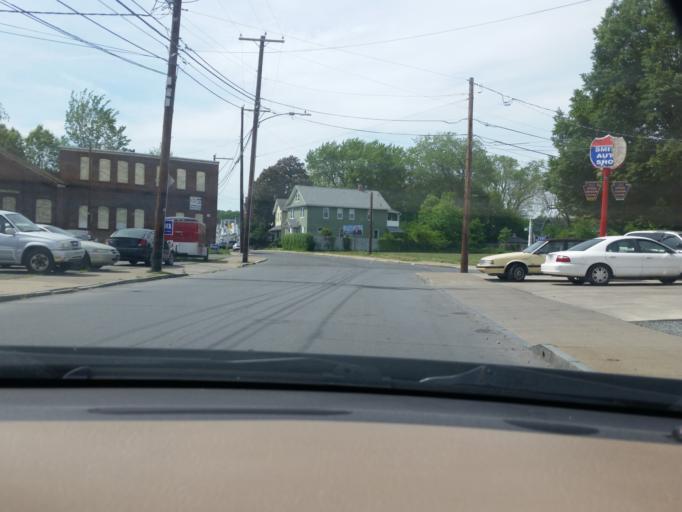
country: US
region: Pennsylvania
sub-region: Luzerne County
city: Wilkes-Barre
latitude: 41.2366
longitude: -75.9003
